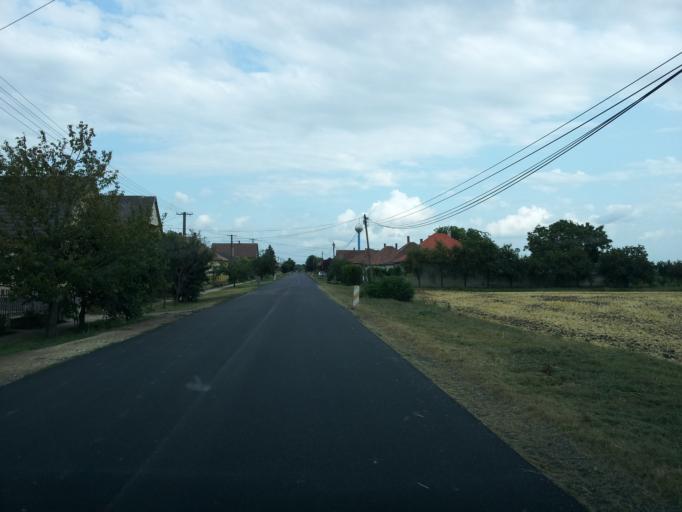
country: HU
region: Fejer
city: Enying
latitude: 46.8950
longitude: 18.2666
